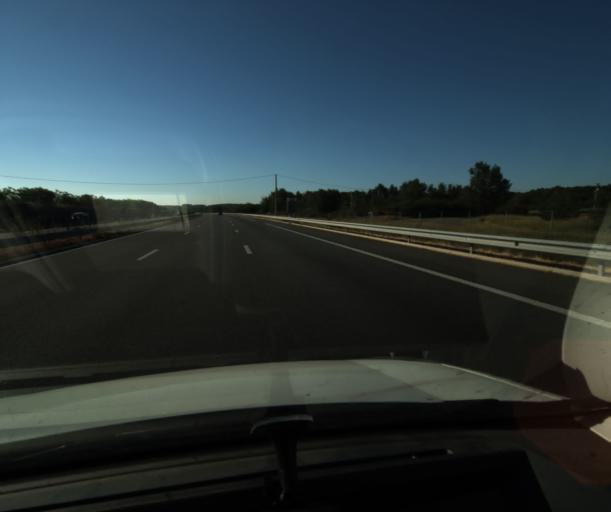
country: FR
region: Midi-Pyrenees
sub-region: Departement du Tarn-et-Garonne
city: Pompignan
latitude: 43.8203
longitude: 1.3491
